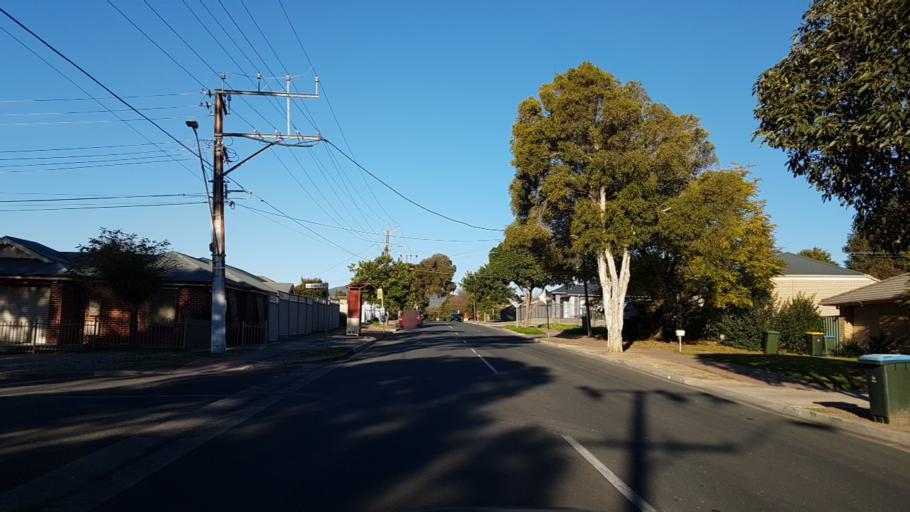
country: AU
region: South Australia
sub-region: Campbelltown
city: Campbelltown
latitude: -34.8769
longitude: 138.6546
